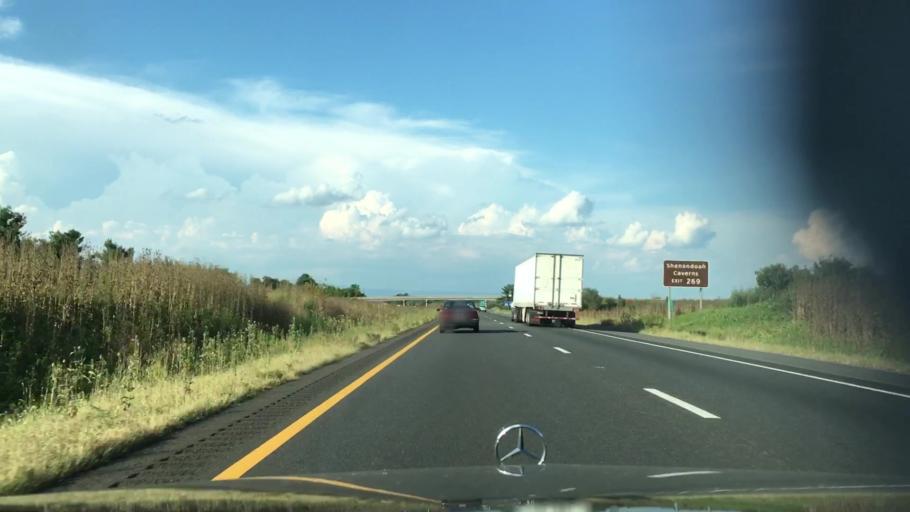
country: US
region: Virginia
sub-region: Shenandoah County
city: New Market
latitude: 38.6793
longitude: -78.6598
